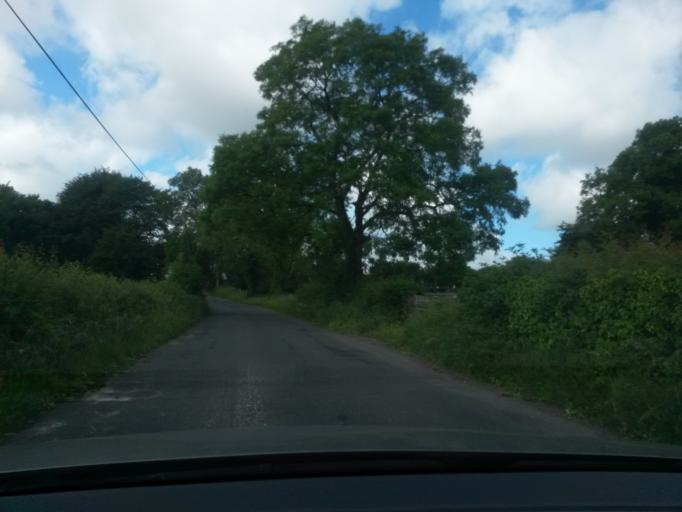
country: IE
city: Ballisodare
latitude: 54.2479
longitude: -8.5018
